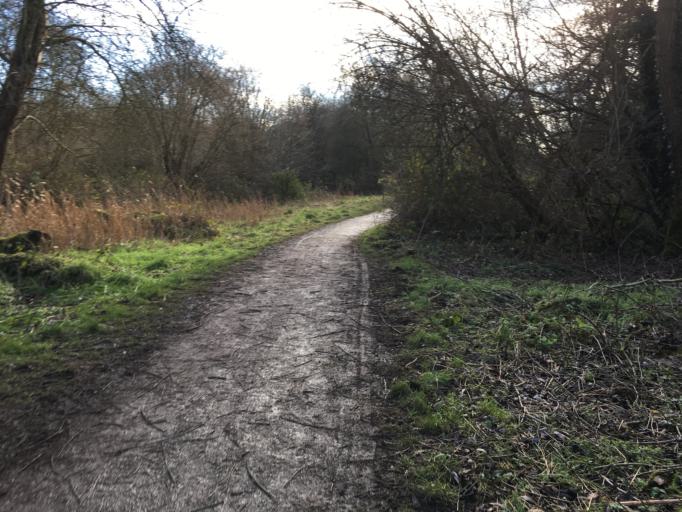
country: GB
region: England
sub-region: Nottinghamshire
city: Gotham
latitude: 52.9108
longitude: -1.2211
